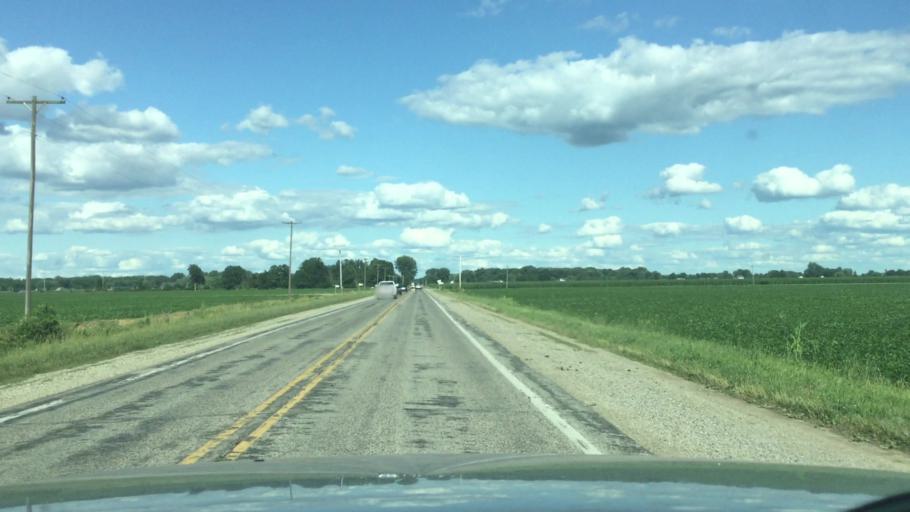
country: US
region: Michigan
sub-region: Saginaw County
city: Shields
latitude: 43.3796
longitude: -84.0908
